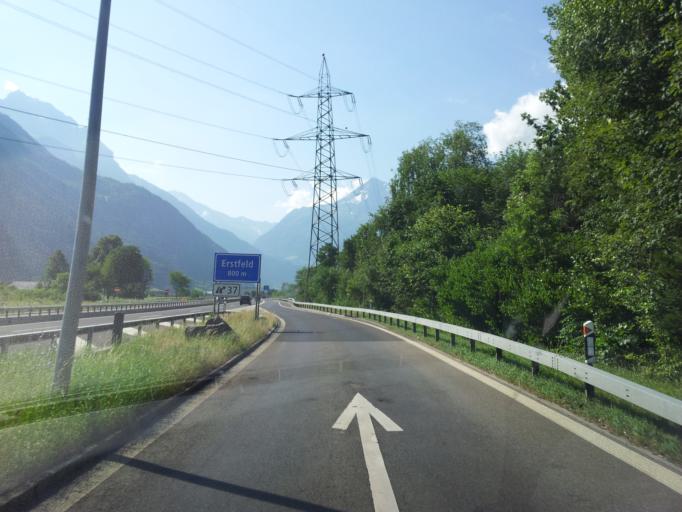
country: CH
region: Uri
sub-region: Uri
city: Attinghausen
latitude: 46.8458
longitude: 8.6329
